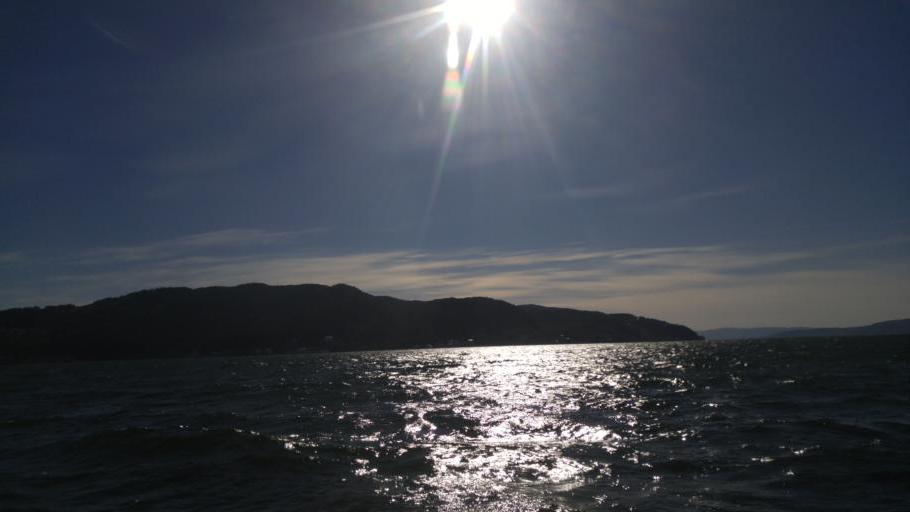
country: NO
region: Sor-Trondelag
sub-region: Trondheim
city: Trondheim
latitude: 63.4464
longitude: 10.3901
